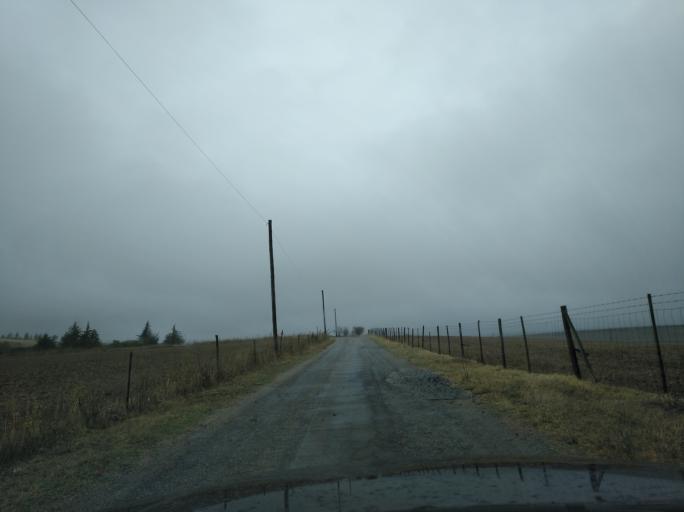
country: PT
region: Portalegre
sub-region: Campo Maior
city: Campo Maior
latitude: 38.9807
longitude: -7.0921
